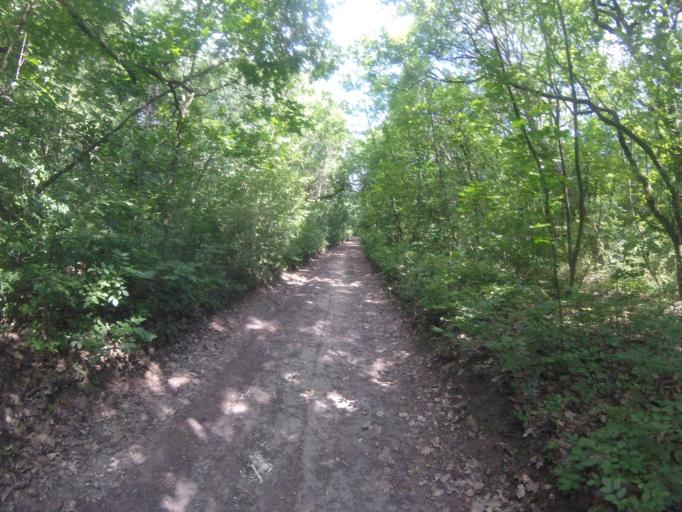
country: HU
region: Fejer
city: Szarliget
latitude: 47.4859
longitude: 18.4923
